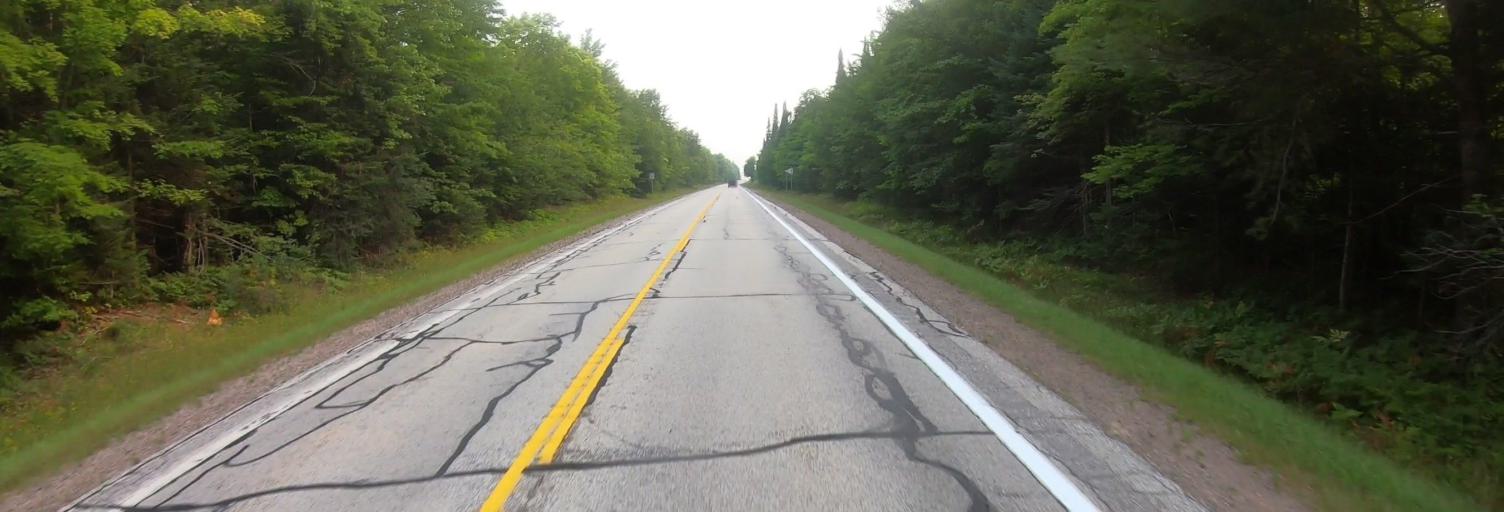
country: US
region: Michigan
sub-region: Luce County
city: Newberry
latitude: 46.4896
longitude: -85.0991
